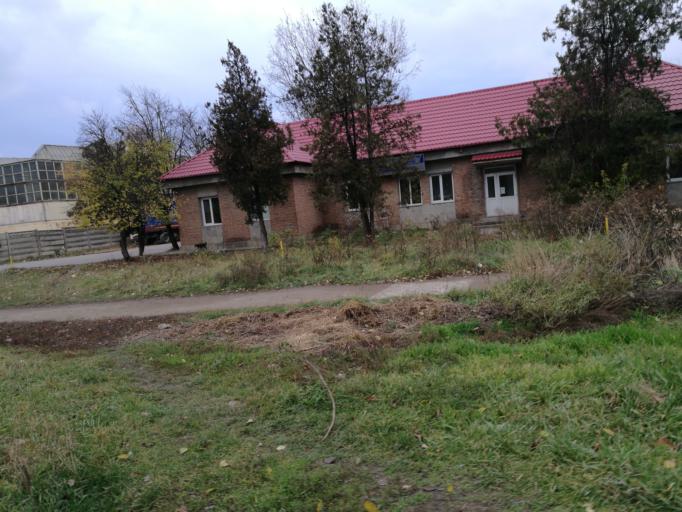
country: RO
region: Suceava
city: Suceava
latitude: 47.6674
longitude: 26.2717
